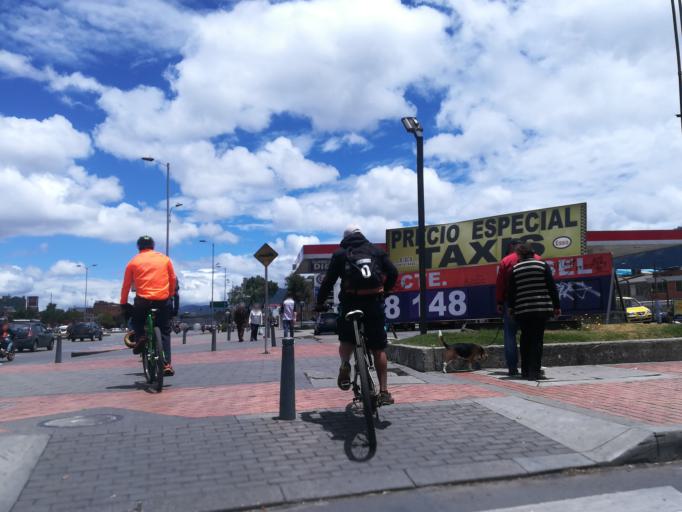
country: CO
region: Bogota D.C.
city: Bogota
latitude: 4.6020
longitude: -74.1018
